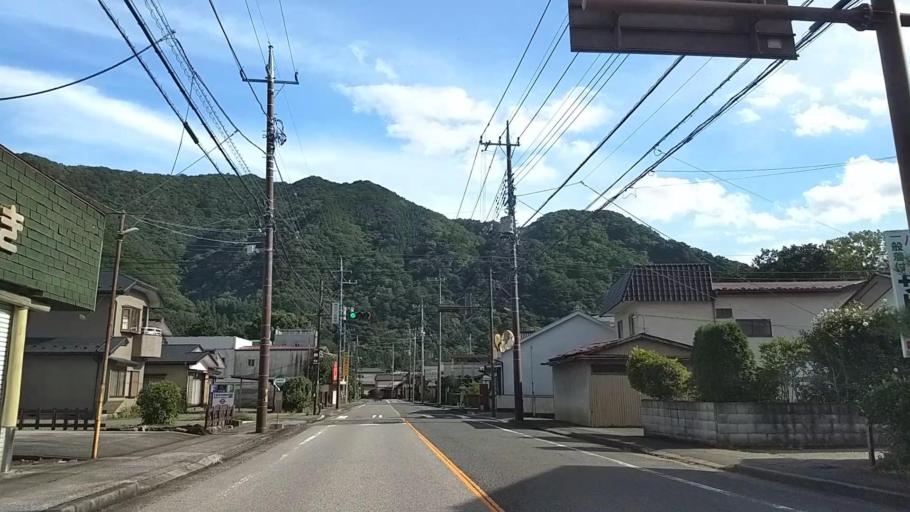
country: JP
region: Tochigi
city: Imaichi
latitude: 36.8542
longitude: 139.7311
